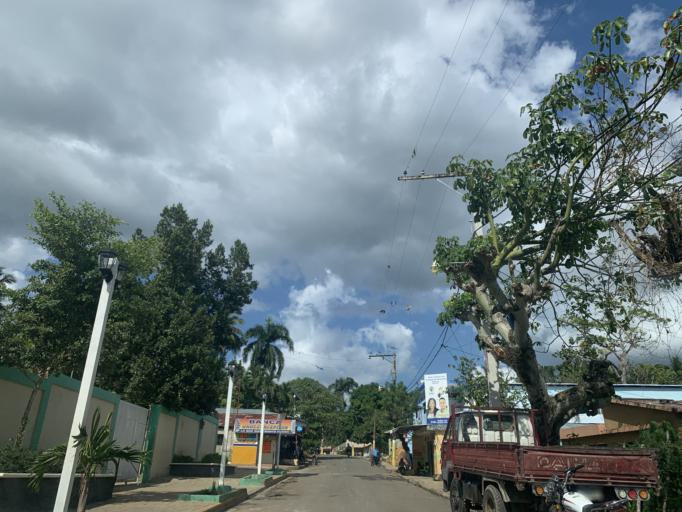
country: DO
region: Monte Plata
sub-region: Yamasa
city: Yamasa
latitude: 18.7739
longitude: -70.0300
